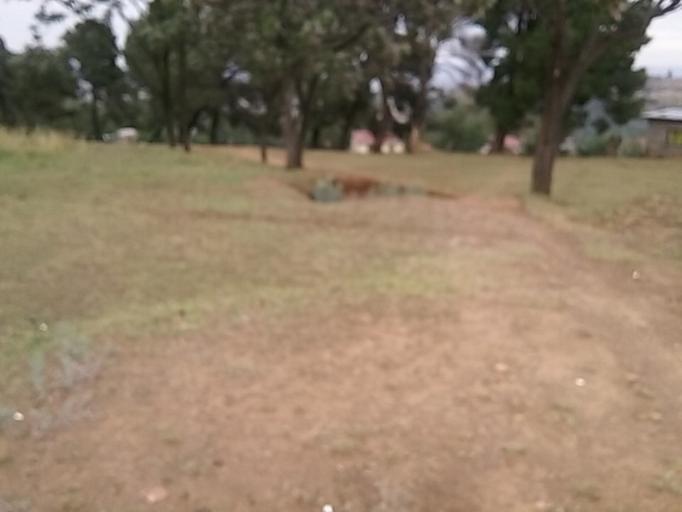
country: LS
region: Berea
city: Teyateyaneng
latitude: -29.1436
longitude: 27.7402
